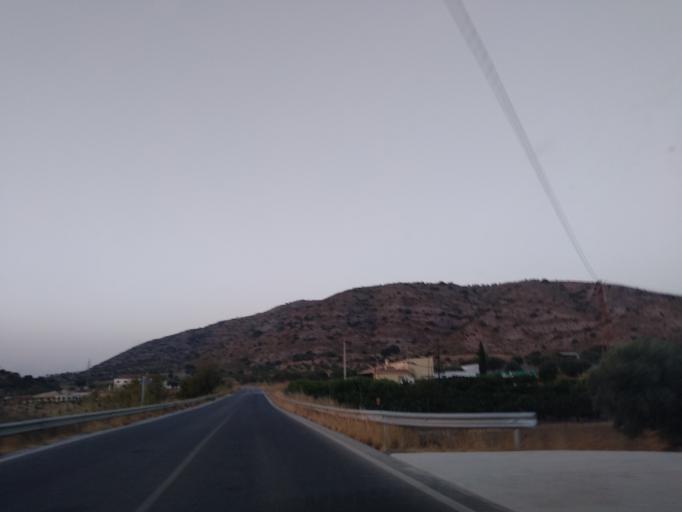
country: ES
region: Andalusia
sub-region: Provincia de Malaga
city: Cartama
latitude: 36.6873
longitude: -4.6524
